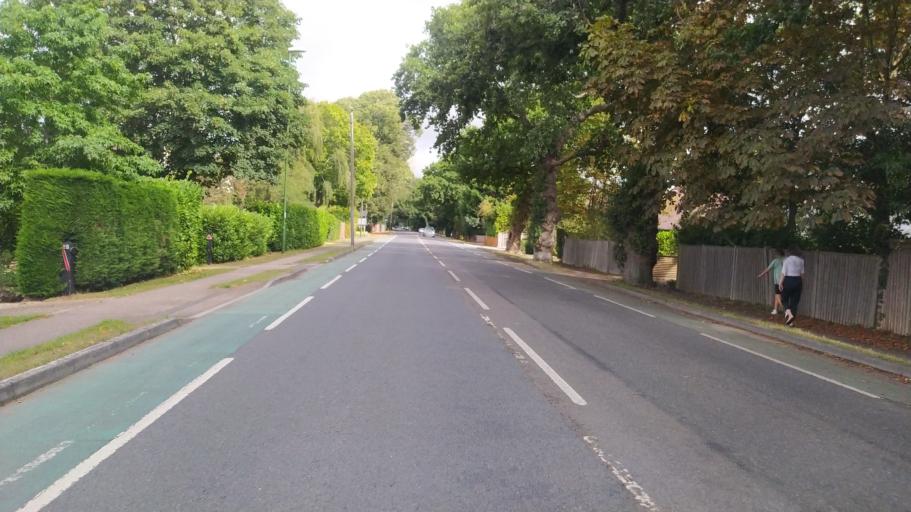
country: GB
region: England
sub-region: West Sussex
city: Chichester
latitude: 50.8560
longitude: -0.7825
